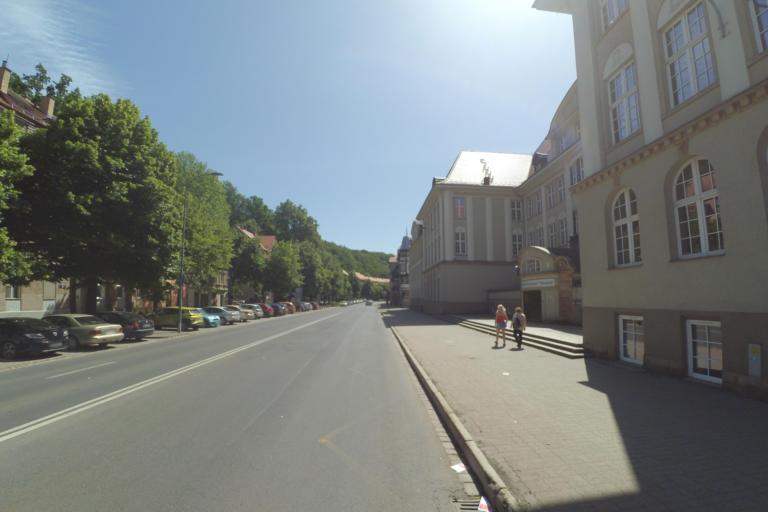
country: PL
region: Lower Silesian Voivodeship
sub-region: Powiat walbrzyski
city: Walbrzych
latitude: 50.7707
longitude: 16.2781
